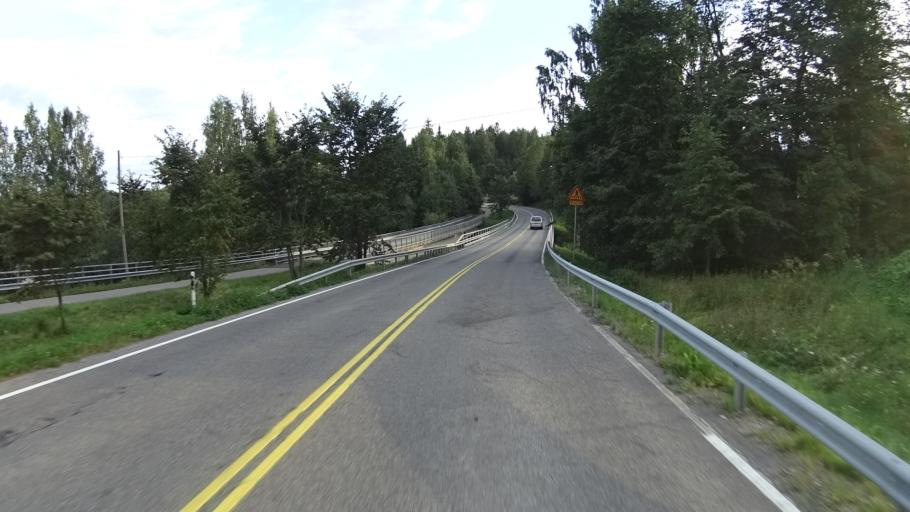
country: FI
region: Uusimaa
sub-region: Helsinki
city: Nurmijaervi
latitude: 60.3446
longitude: 24.8662
